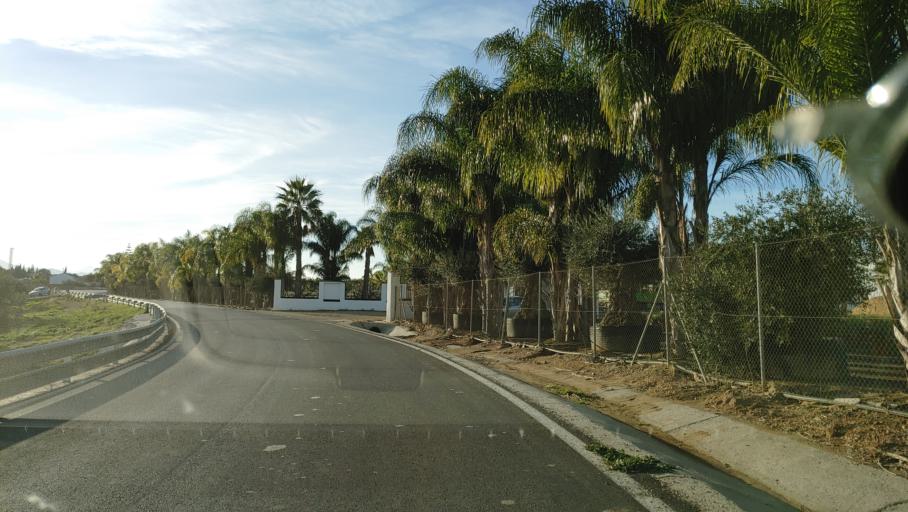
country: ES
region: Andalusia
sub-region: Provincia de Malaga
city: Cartama
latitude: 36.6791
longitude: -4.6244
